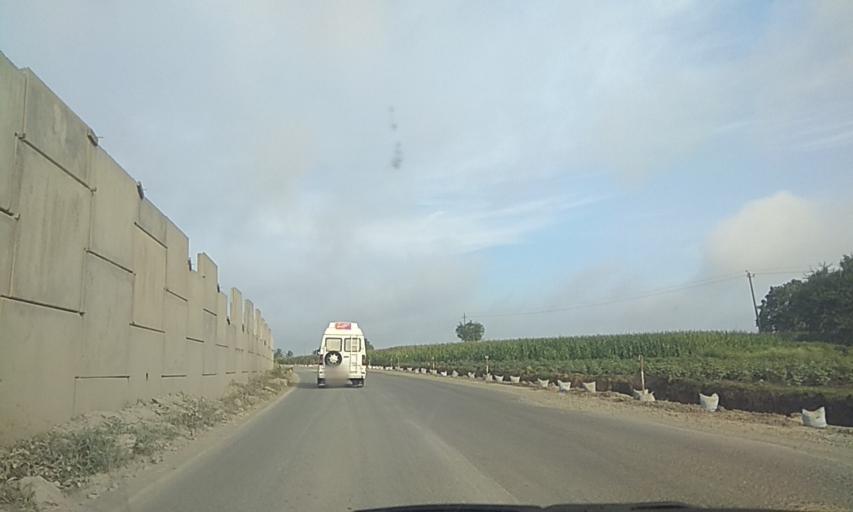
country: IN
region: Karnataka
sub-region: Haveri
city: Haveri
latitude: 14.7608
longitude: 75.4388
